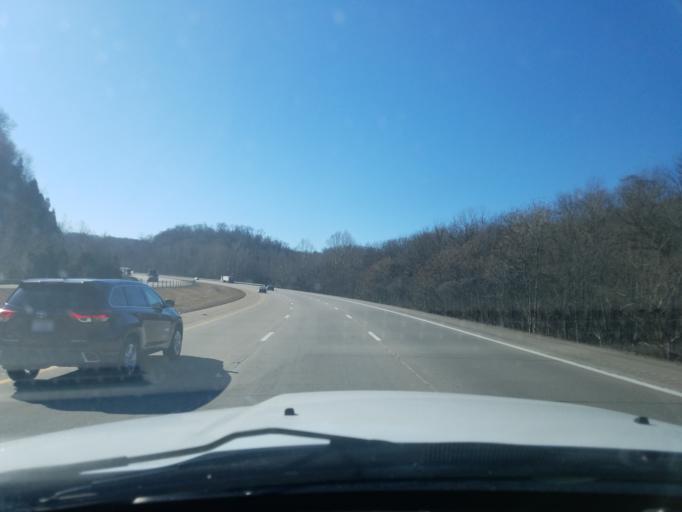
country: US
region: Kentucky
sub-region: Bullitt County
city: Lebanon Junction
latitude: 37.7695
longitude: -85.7899
